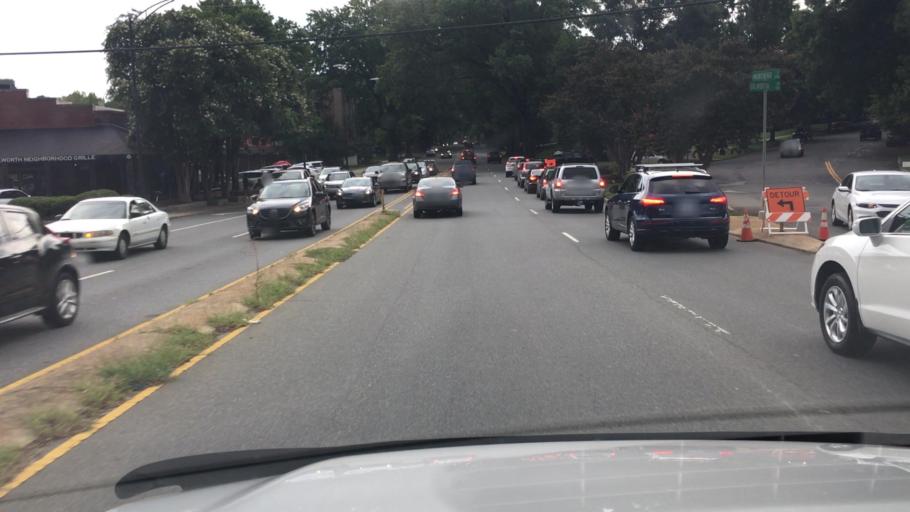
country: US
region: North Carolina
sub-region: Mecklenburg County
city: Charlotte
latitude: 35.2137
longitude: -80.8444
